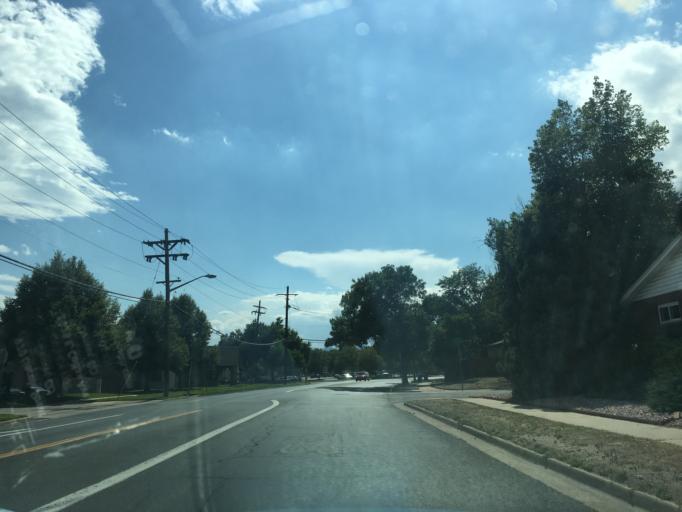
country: US
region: Colorado
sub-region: Arapahoe County
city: Sheridan
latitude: 39.6566
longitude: -105.0501
